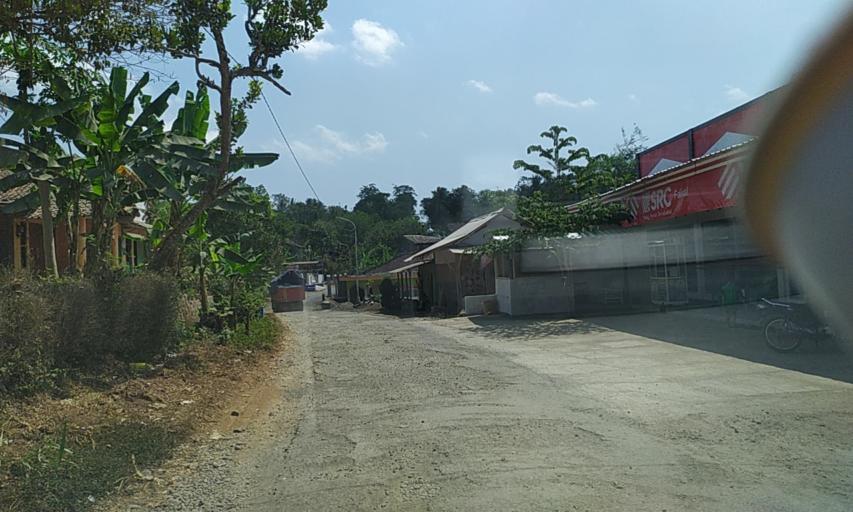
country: ID
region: Central Java
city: Karanggintung
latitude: -7.4581
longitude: 108.8601
